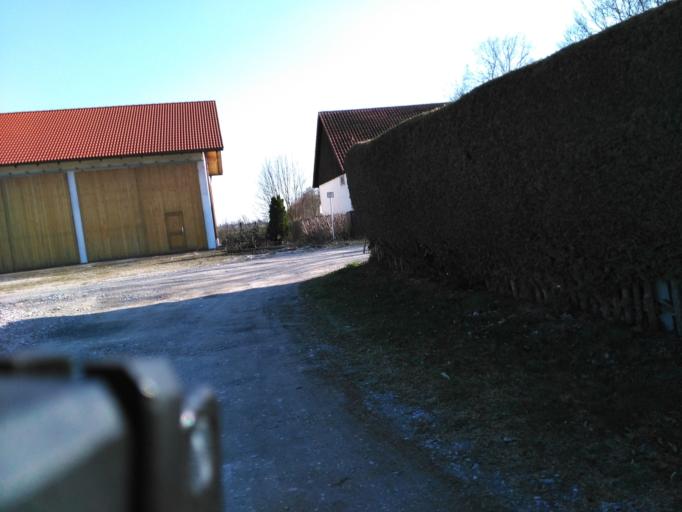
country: DE
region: Bavaria
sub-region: Upper Bavaria
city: Mammendorf
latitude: 48.2059
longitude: 11.1613
